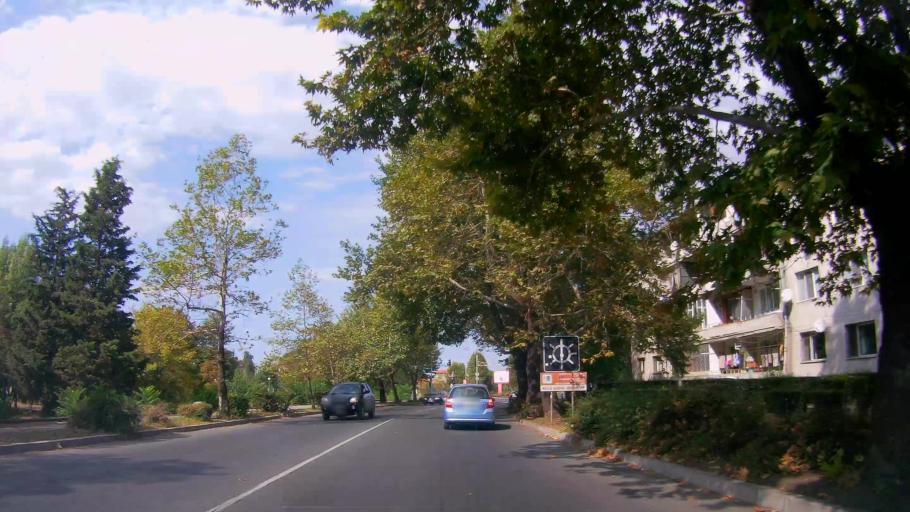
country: BG
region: Burgas
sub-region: Obshtina Aytos
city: Aytos
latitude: 42.6986
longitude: 27.2506
